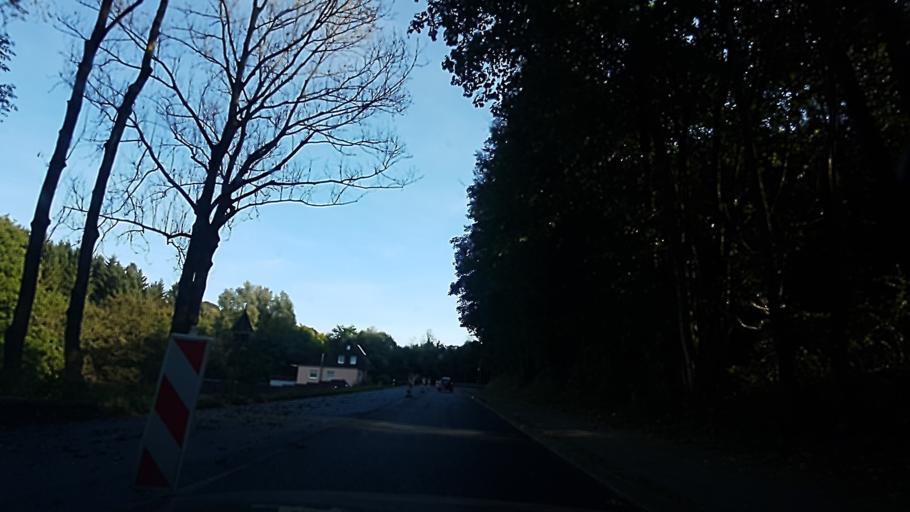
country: DE
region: North Rhine-Westphalia
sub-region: Regierungsbezirk Koln
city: Marienheide
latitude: 51.0922
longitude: 7.5261
